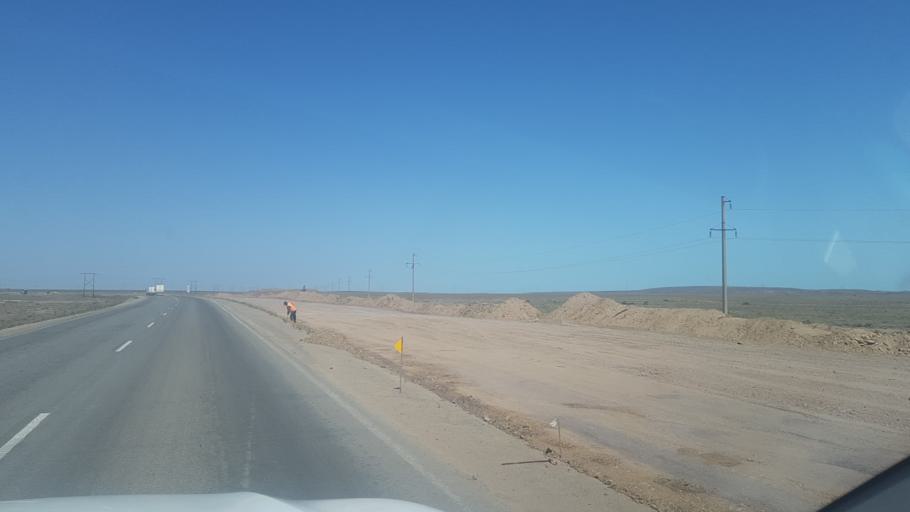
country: KZ
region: Qaraghandy
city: Balqash
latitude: 46.6561
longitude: 74.3998
